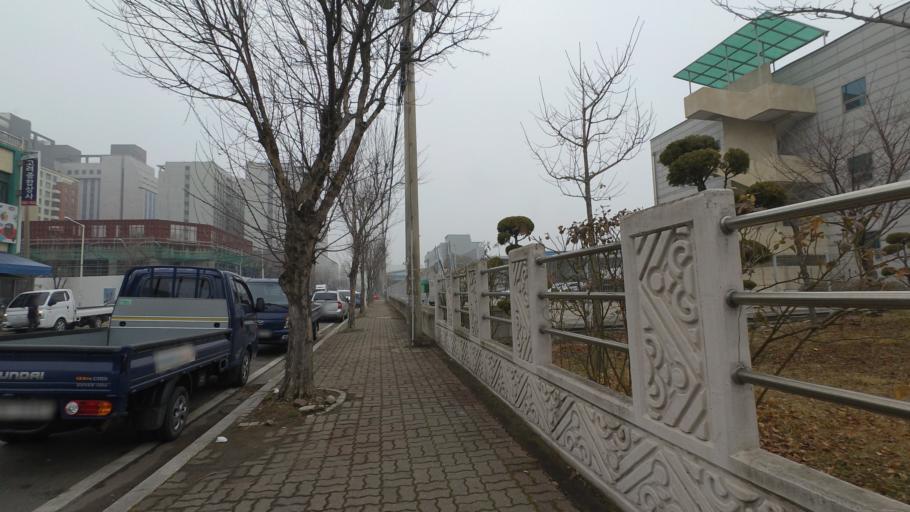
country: KR
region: Chungcheongnam-do
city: Tangjin
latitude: 36.9756
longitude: 126.8452
